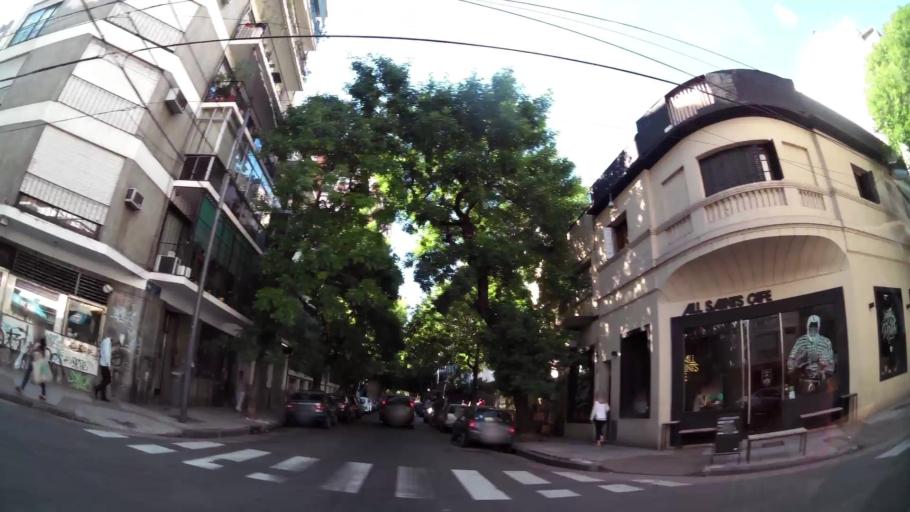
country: AR
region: Buenos Aires F.D.
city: Colegiales
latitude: -34.5608
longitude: -58.4593
